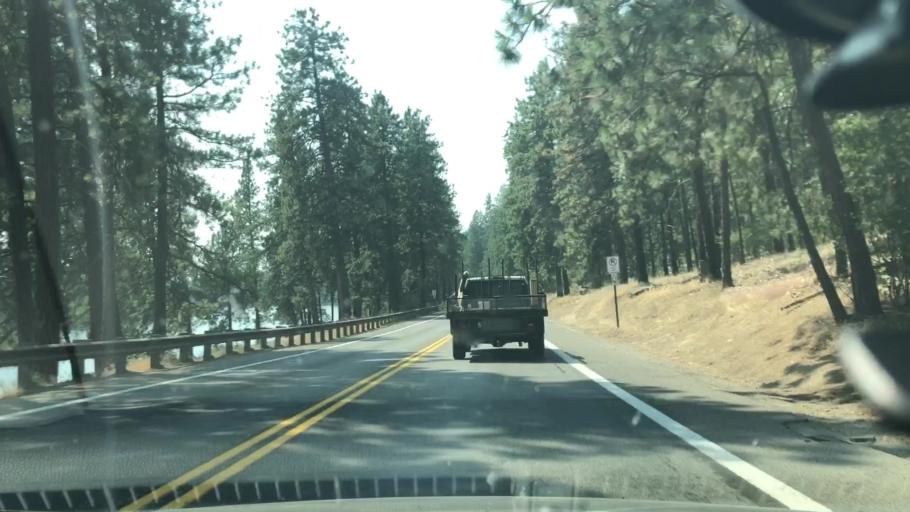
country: US
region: Washington
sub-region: Spokane County
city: Millwood
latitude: 47.6948
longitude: -117.3088
